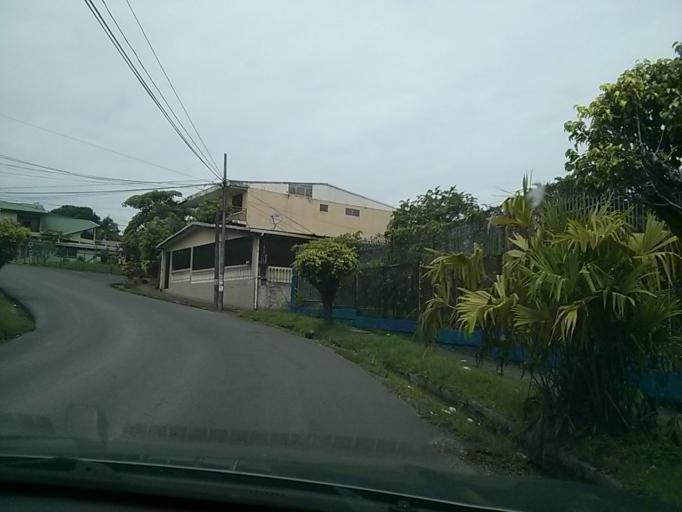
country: CR
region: Limon
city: Limon
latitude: 9.9992
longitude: -83.0342
